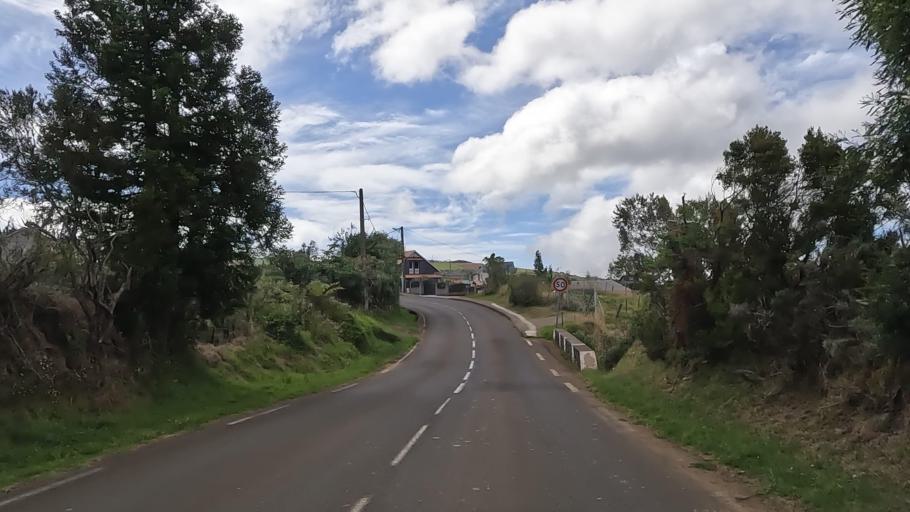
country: RE
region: Reunion
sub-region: Reunion
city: Le Tampon
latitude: -21.2446
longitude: 55.5910
